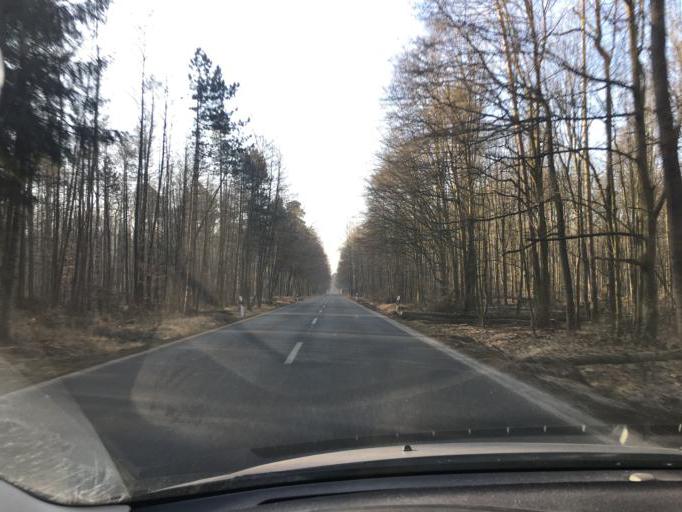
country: DE
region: Thuringia
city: Langenleuba-Niederhain
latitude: 50.9877
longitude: 12.5637
